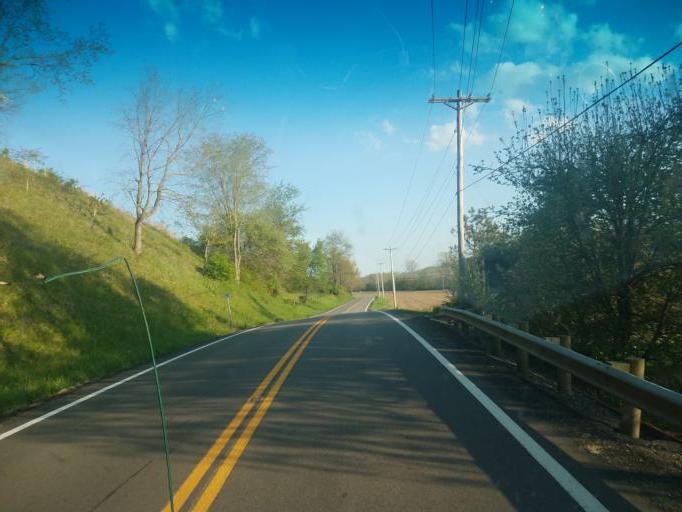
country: US
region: Ohio
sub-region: Holmes County
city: Millersburg
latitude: 40.5115
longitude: -81.9908
